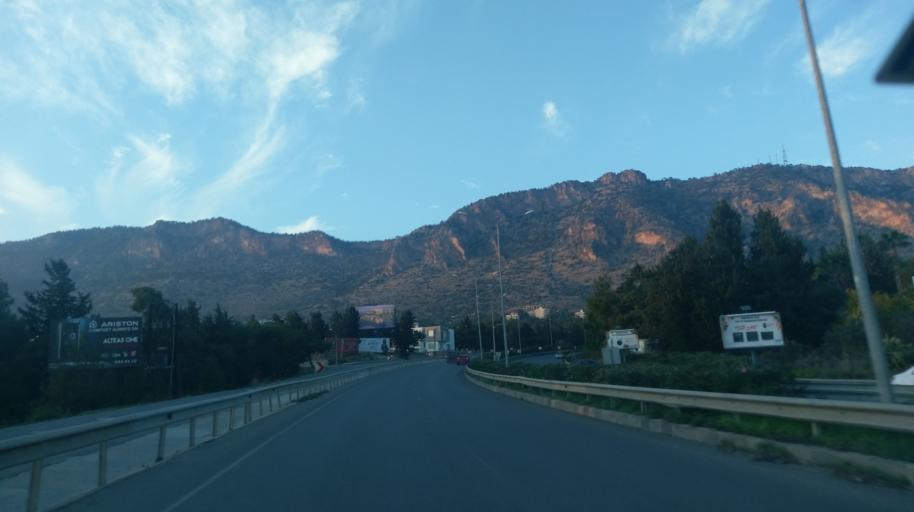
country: CY
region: Keryneia
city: Kyrenia
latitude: 35.2892
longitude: 33.2765
